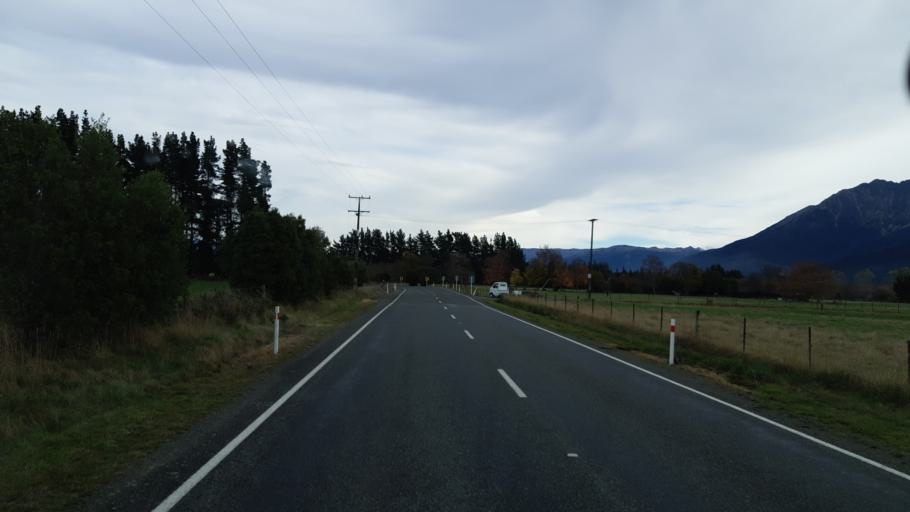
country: NZ
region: Tasman
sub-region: Tasman District
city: Brightwater
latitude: -41.6285
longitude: 173.3368
